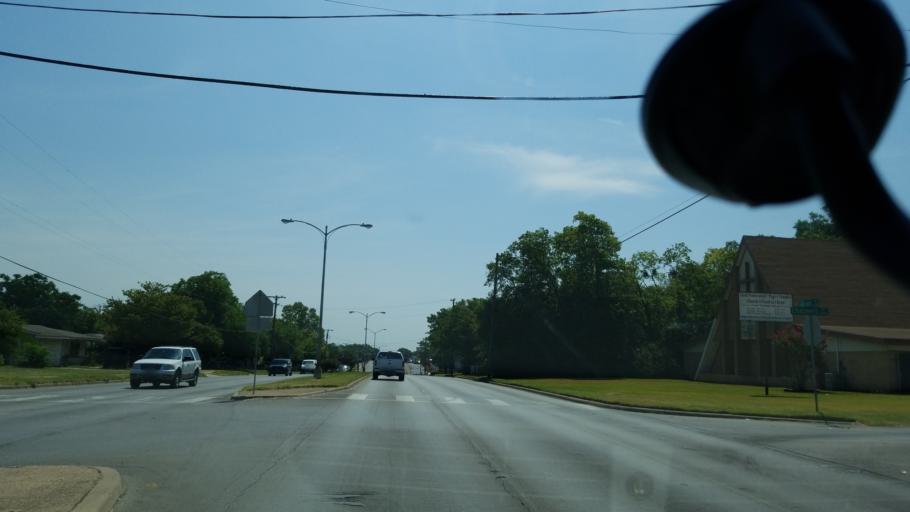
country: US
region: Texas
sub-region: Dallas County
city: Cockrell Hill
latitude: 32.7203
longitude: -96.8626
